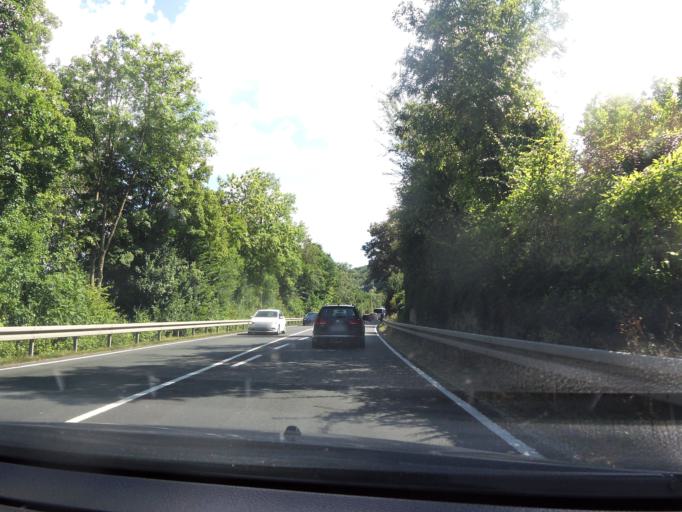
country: DE
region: Bavaria
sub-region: Regierungsbezirk Unterfranken
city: Zell am Main
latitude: 49.8053
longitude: 9.8760
